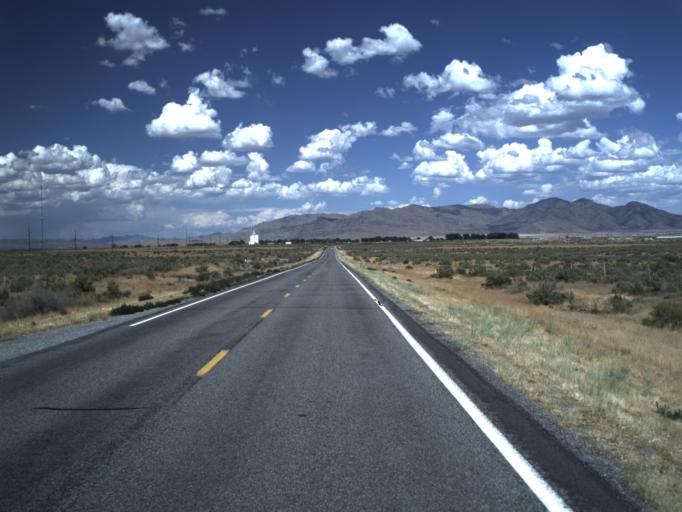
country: US
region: Utah
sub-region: Millard County
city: Delta
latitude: 39.4955
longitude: -112.3974
